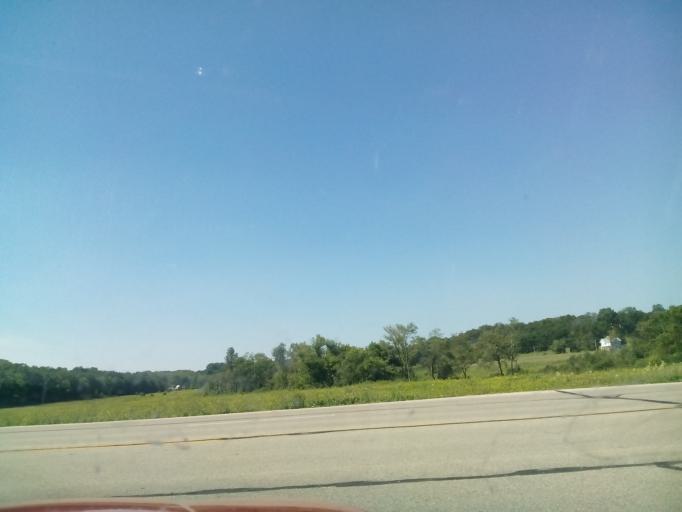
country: US
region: Wisconsin
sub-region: Green County
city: New Glarus
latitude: 42.7970
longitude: -89.6324
